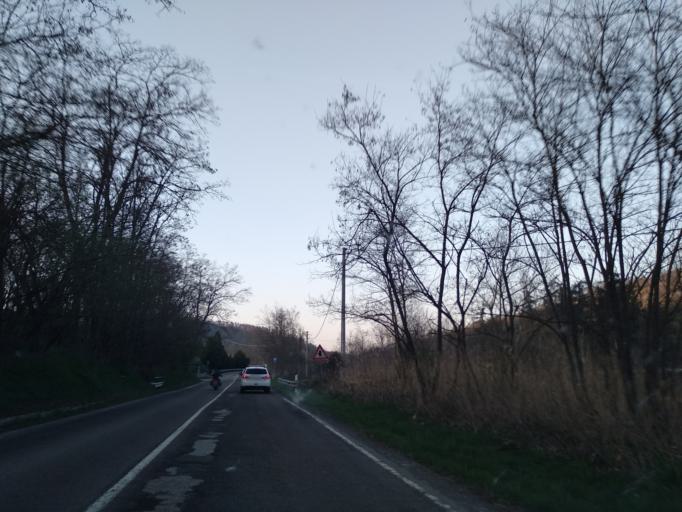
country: IT
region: Emilia-Romagna
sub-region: Provincia di Reggio Emilia
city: Vezzano sul Crostolo
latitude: 44.5710
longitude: 10.5275
